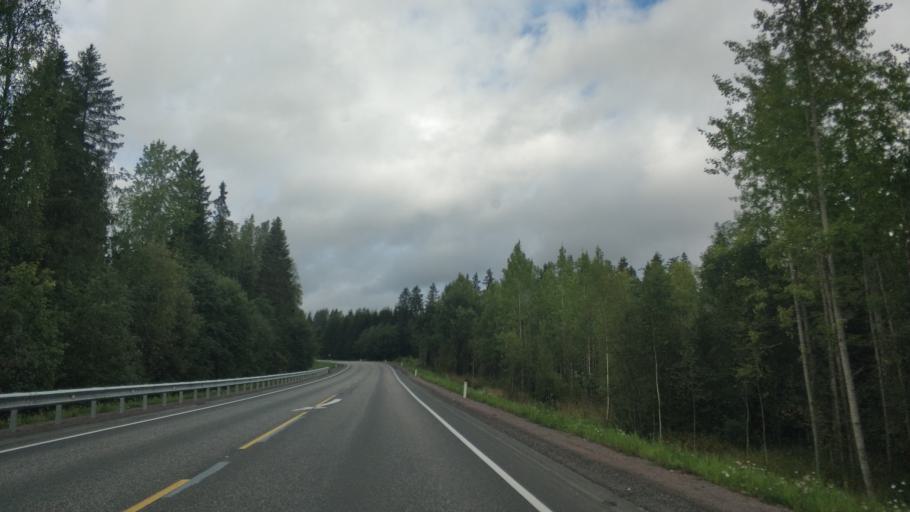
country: RU
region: Republic of Karelia
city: Khelyulya
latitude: 61.7901
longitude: 30.6315
